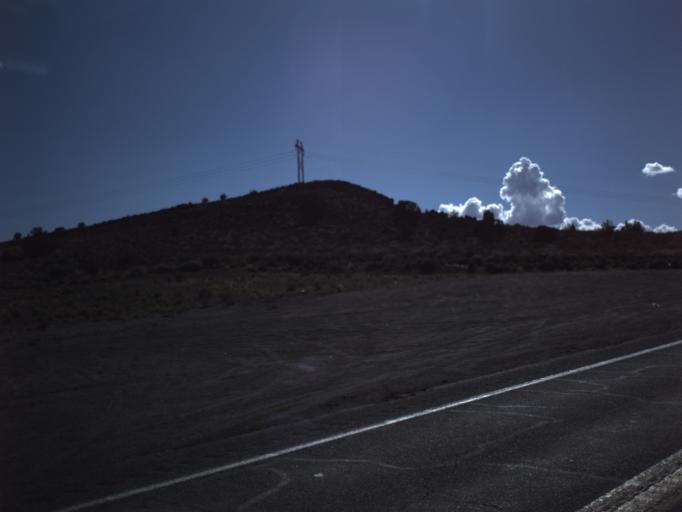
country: US
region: Utah
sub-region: Washington County
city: Toquerville
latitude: 37.2753
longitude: -113.3011
